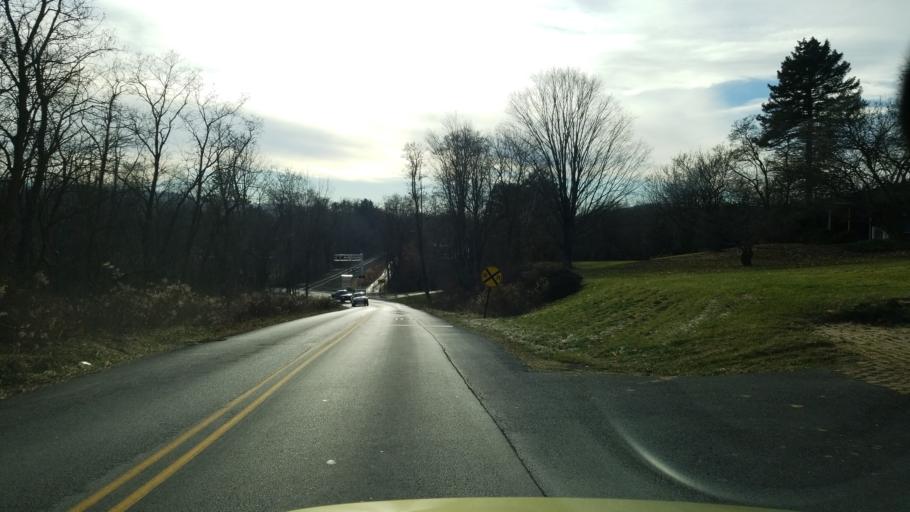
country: US
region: Pennsylvania
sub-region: Clearfield County
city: Hyde
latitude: 41.0144
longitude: -78.4518
